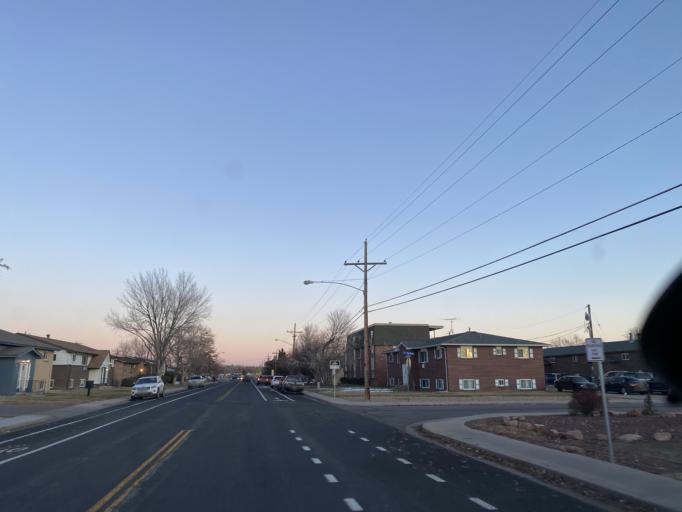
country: US
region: Colorado
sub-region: Adams County
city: Brighton
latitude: 39.9774
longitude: -104.8156
